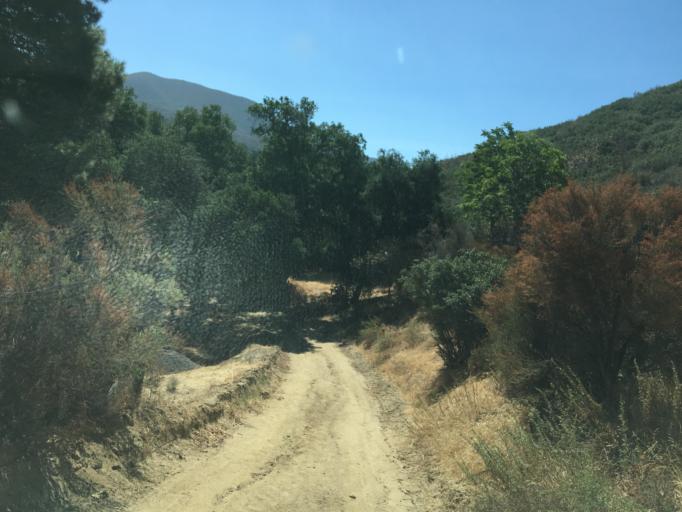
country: US
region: California
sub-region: Los Angeles County
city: Green Valley
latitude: 34.6129
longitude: -118.4007
